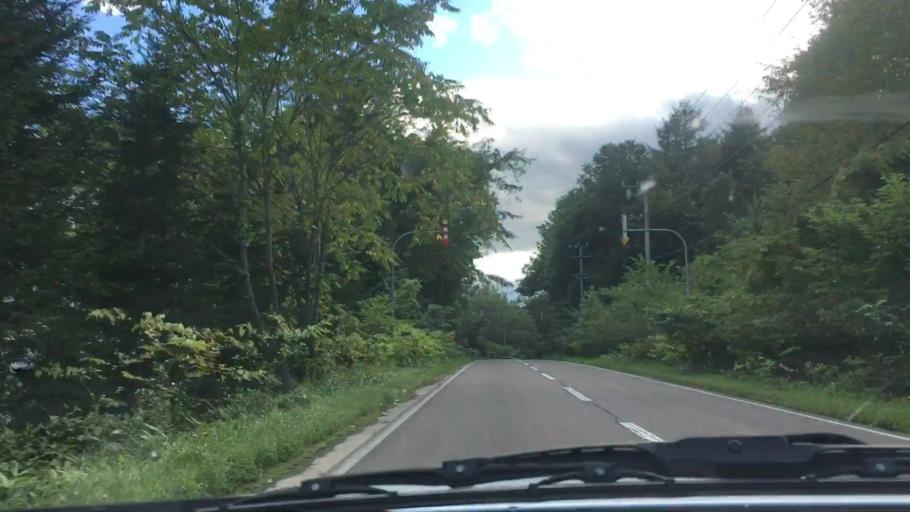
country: JP
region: Hokkaido
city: Otofuke
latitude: 43.1699
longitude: 142.9122
